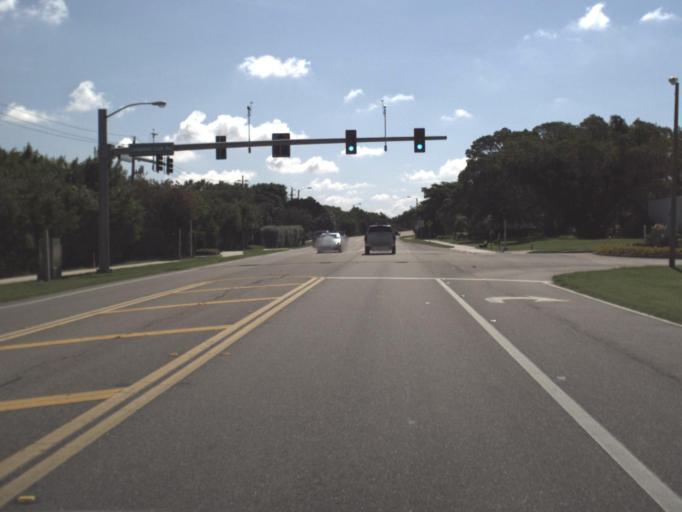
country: US
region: Florida
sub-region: Sarasota County
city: Siesta Key
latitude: 27.3367
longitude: -82.5871
